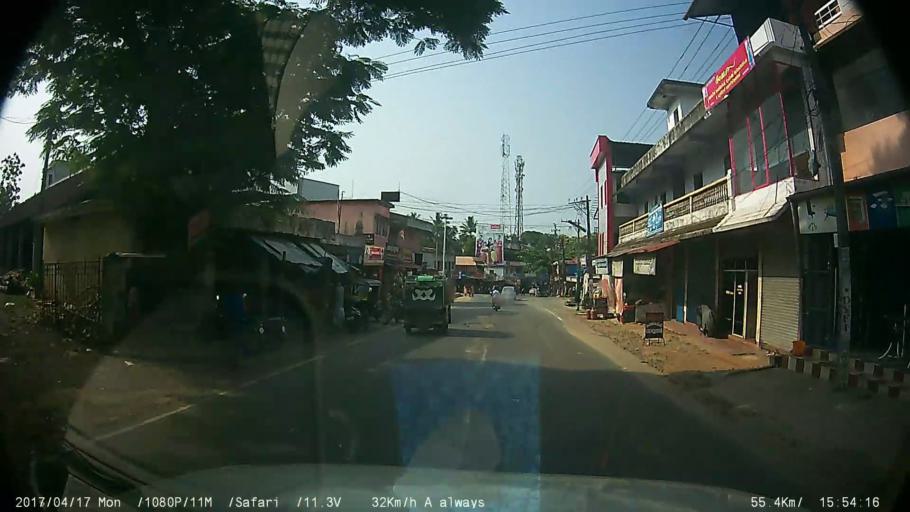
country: IN
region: Kerala
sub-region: Ernakulam
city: Perumbavoor
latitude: 10.0824
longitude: 76.4660
